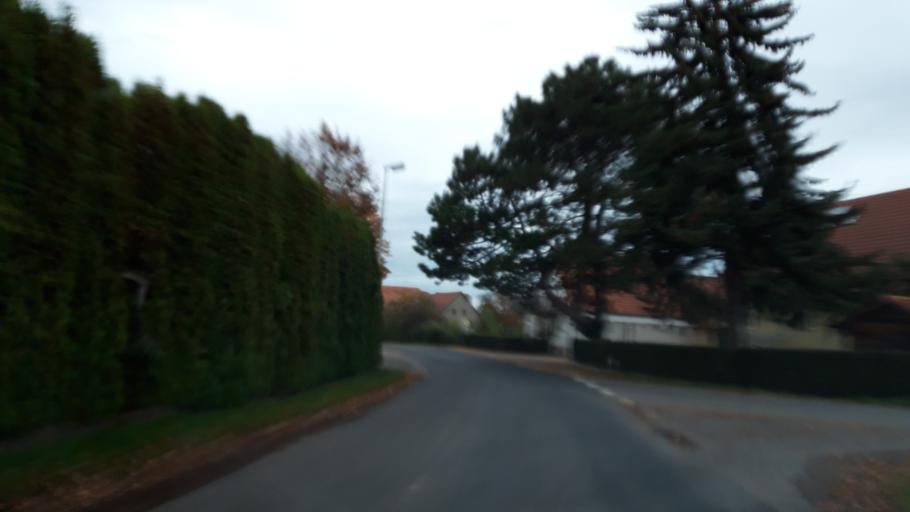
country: DE
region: Bavaria
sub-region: Regierungsbezirk Unterfranken
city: Esselbach
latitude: 49.8118
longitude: 9.5523
